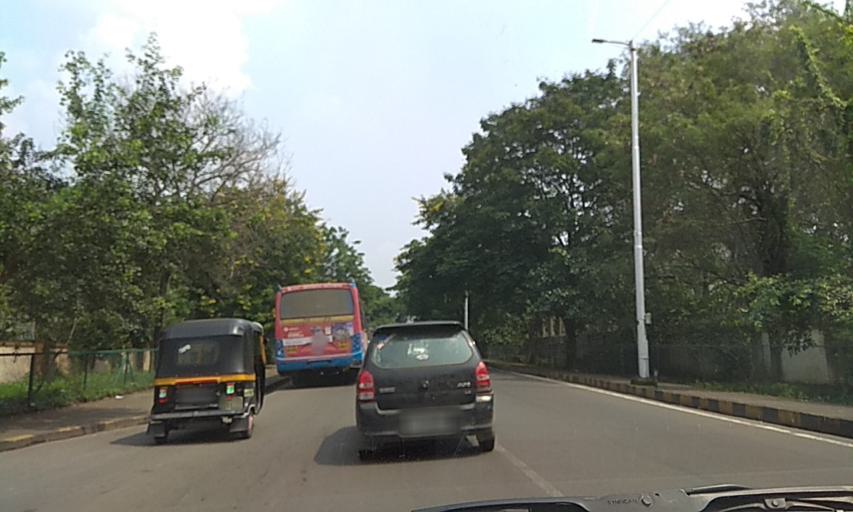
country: IN
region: Maharashtra
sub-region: Pune Division
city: Shivaji Nagar
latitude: 18.5380
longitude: 73.7976
